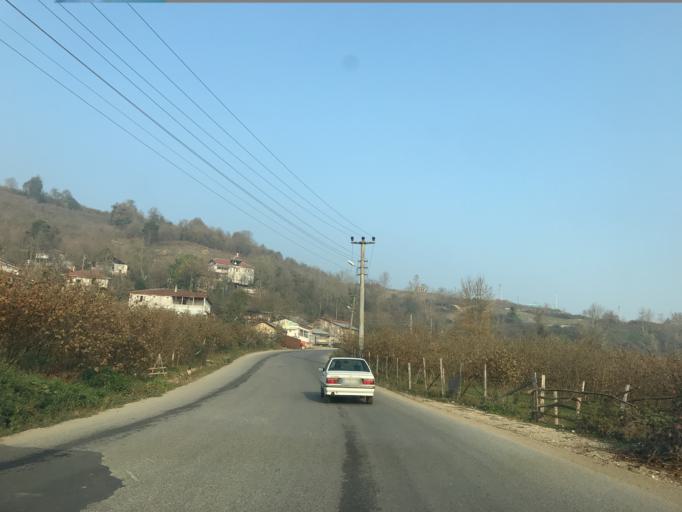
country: TR
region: Duzce
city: Cumayeri
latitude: 40.8877
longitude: 30.9521
